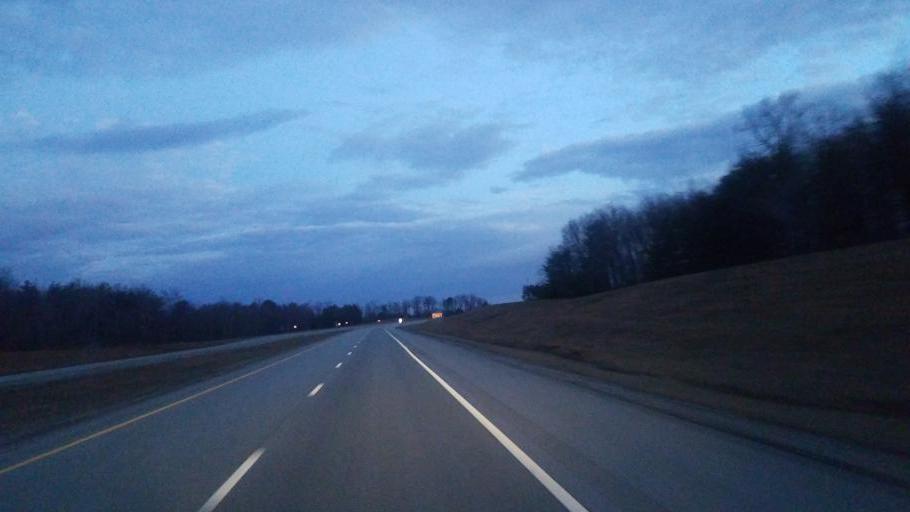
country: US
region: Tennessee
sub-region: Van Buren County
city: Spencer
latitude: 35.6198
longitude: -85.4753
